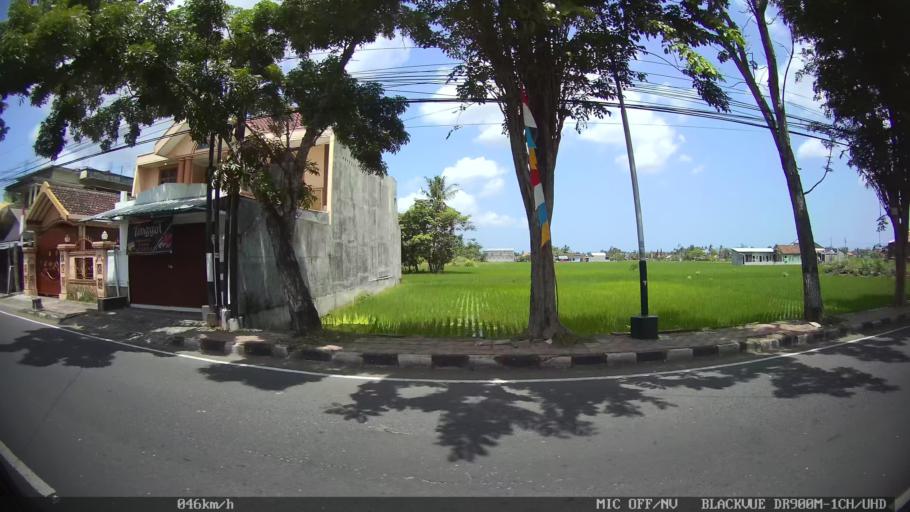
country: ID
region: Daerah Istimewa Yogyakarta
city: Bantul
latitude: -7.8920
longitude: 110.3301
